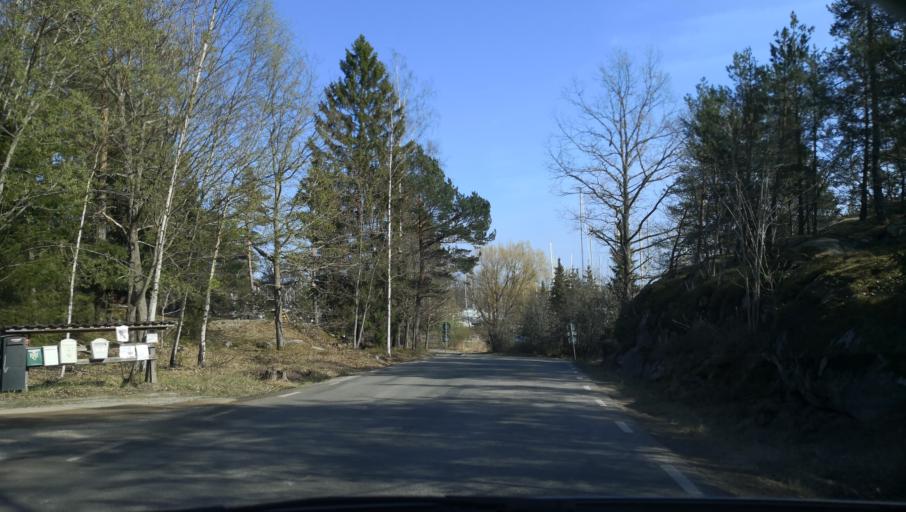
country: SE
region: Stockholm
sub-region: Varmdo Kommun
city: Holo
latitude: 59.3025
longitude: 18.6469
